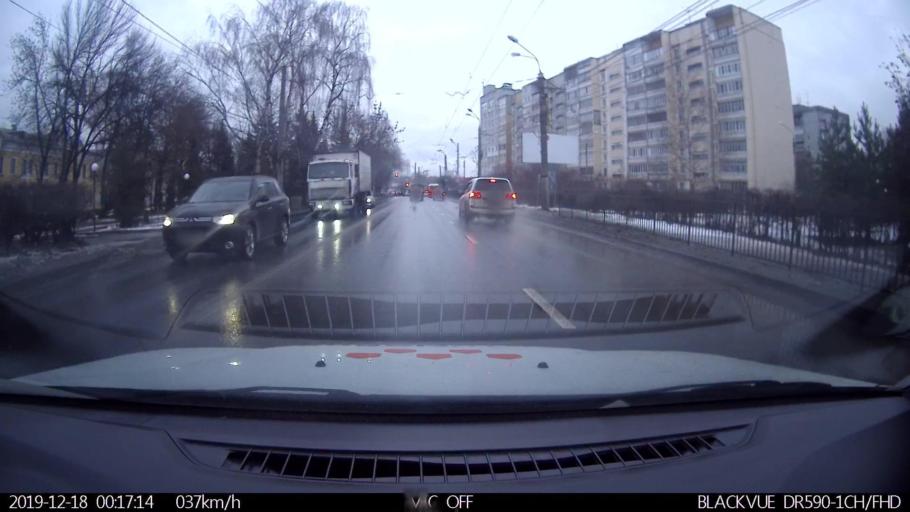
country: RU
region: Nizjnij Novgorod
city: Nizhniy Novgorod
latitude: 56.3250
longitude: 43.8796
